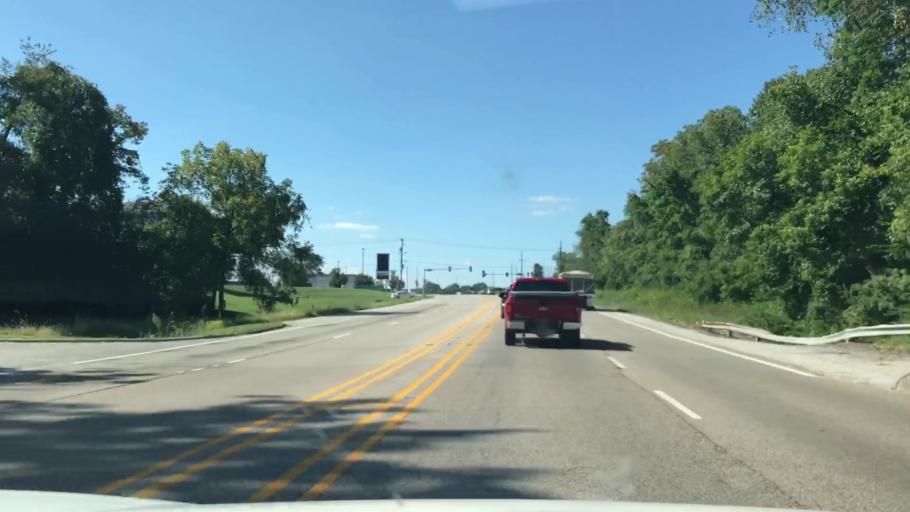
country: US
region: Illinois
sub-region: Saint Clair County
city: Swansea
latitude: 38.5433
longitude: -90.0490
